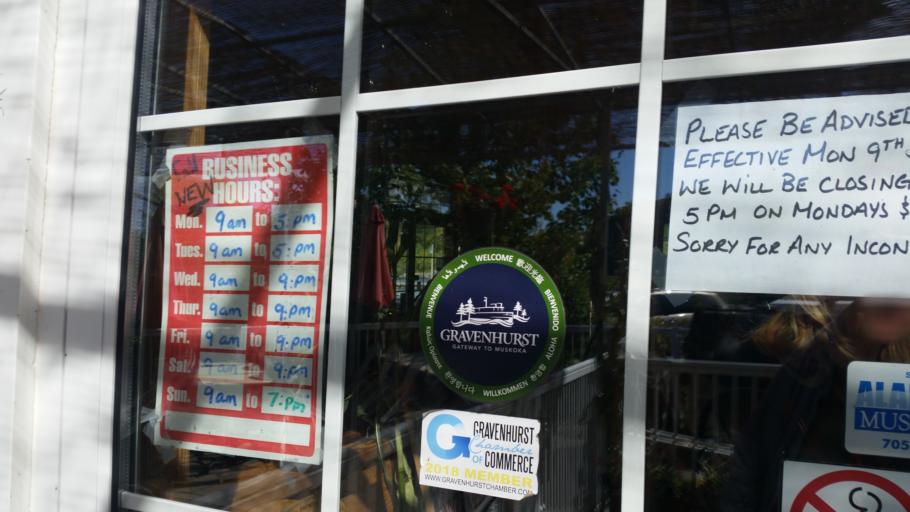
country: CA
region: Ontario
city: Gravenhurst
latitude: 44.9203
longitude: -79.3843
